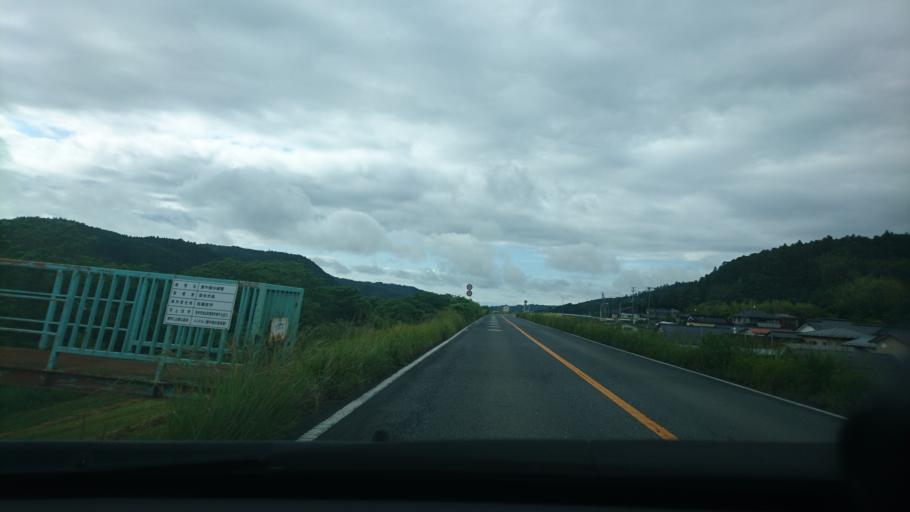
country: JP
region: Miyagi
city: Wakuya
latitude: 38.6213
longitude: 141.2964
